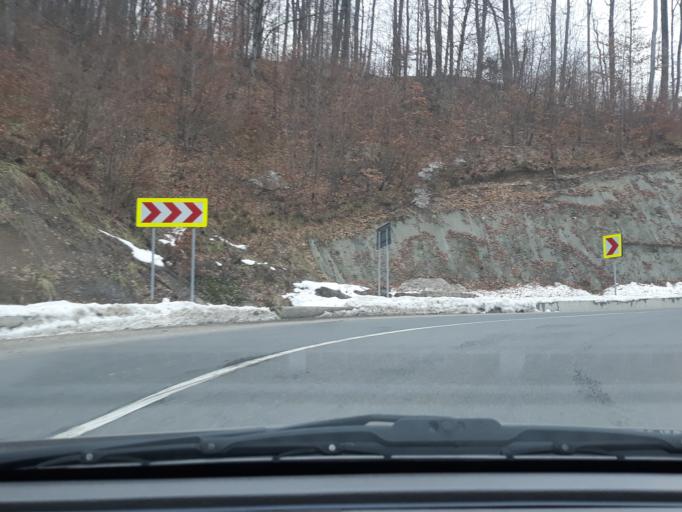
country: RO
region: Bihor
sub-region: Oras Alesd
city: Padurea Neagra
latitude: 47.1260
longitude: 22.4184
